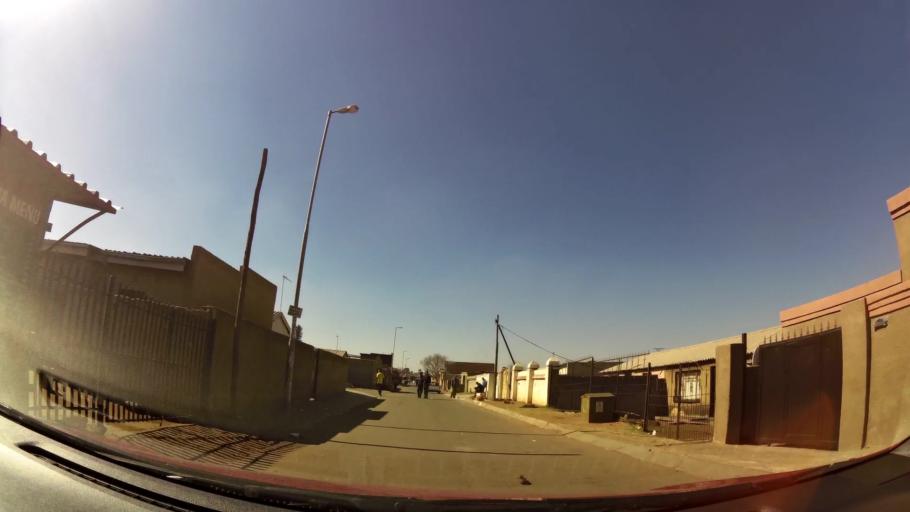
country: ZA
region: Gauteng
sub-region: City of Johannesburg Metropolitan Municipality
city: Soweto
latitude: -26.2400
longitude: 27.8451
